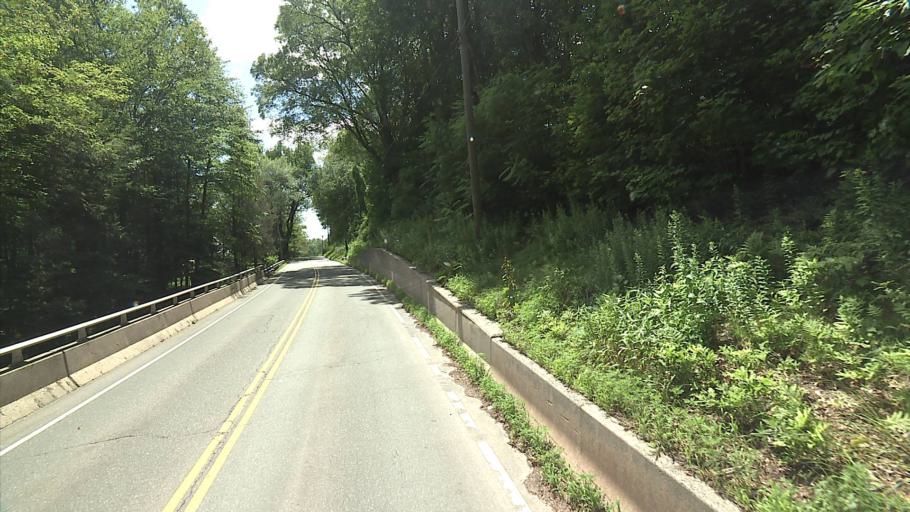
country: US
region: Connecticut
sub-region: Windham County
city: Quinebaug
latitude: 42.0168
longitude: -71.9633
